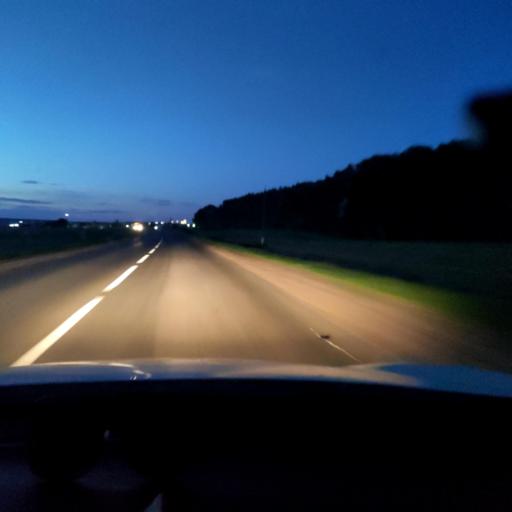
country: RU
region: Tatarstan
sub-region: Alekseyevskiy Rayon
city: Alekseyevskoye
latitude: 55.4182
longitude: 49.8708
